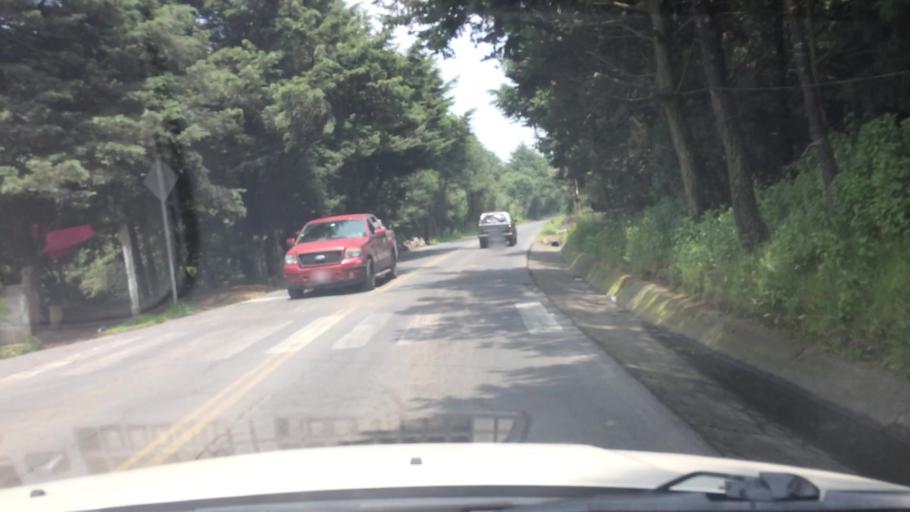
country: MX
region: Mexico City
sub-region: Tlalpan
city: Lomas de Tepemecatl
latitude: 19.2320
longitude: -99.2183
